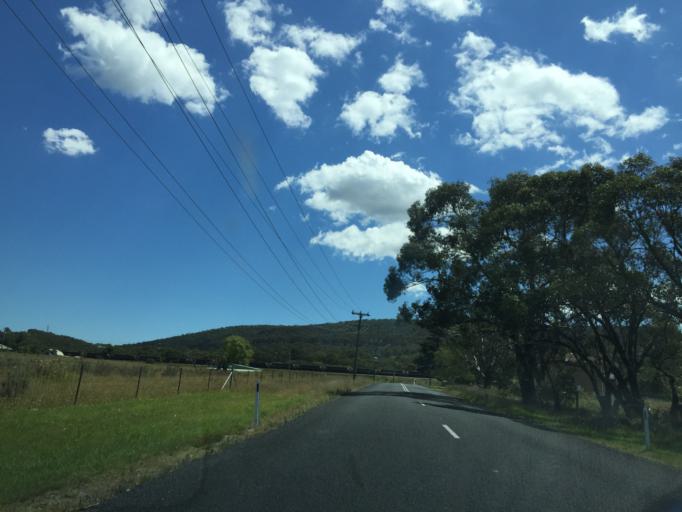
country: AU
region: New South Wales
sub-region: Lithgow
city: Lithgow
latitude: -33.4392
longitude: 150.1165
